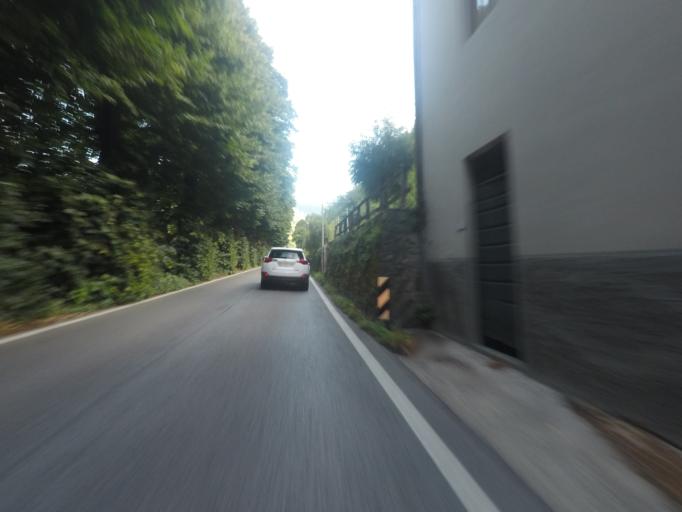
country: IT
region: Tuscany
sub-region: Provincia di Lucca
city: Bagni di Lucca
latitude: 44.0014
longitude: 10.5599
